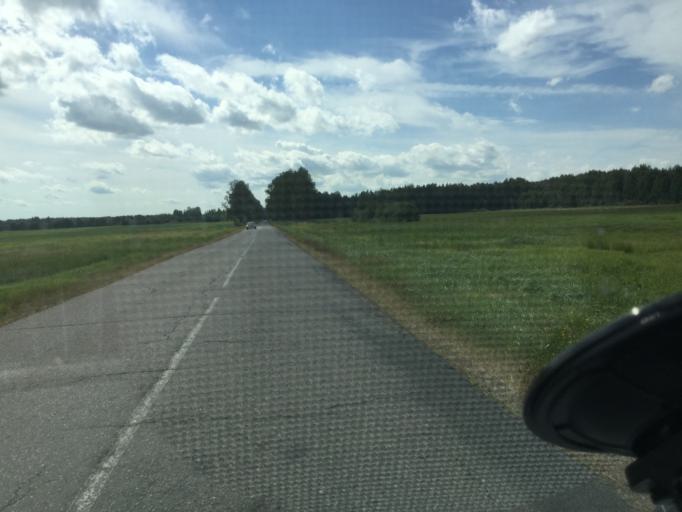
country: BY
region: Vitebsk
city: Chashniki
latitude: 55.3087
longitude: 29.4041
